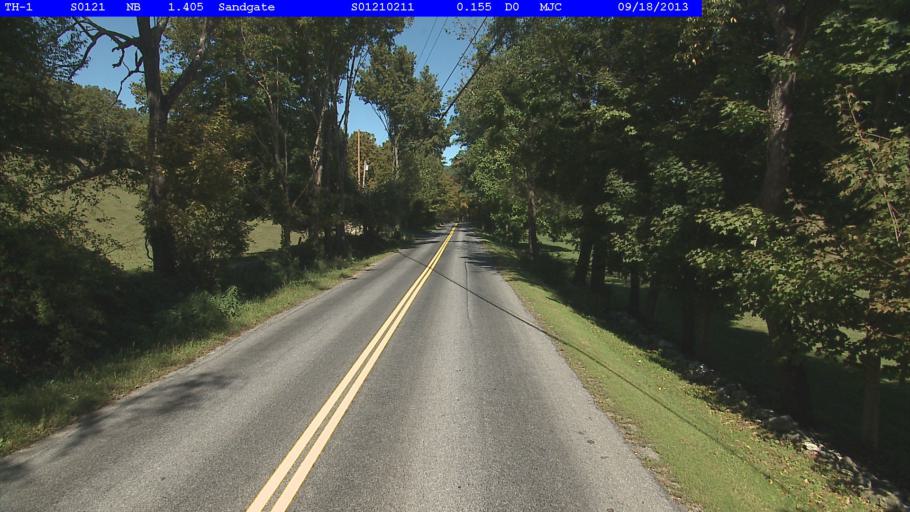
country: US
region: Vermont
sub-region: Bennington County
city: Arlington
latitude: 43.1228
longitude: -73.2069
